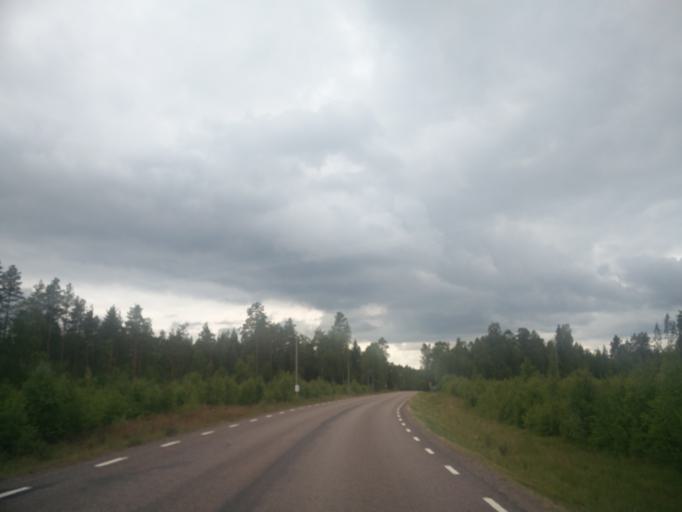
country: SE
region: Vaermland
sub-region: Arvika Kommun
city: Arvika
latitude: 59.9376
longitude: 12.6739
